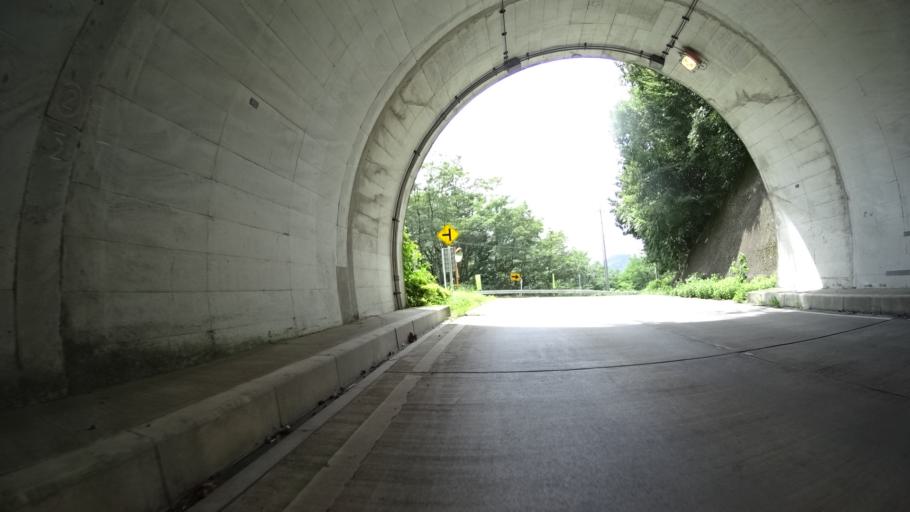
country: JP
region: Yamanashi
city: Nirasaki
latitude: 35.8683
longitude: 138.5052
